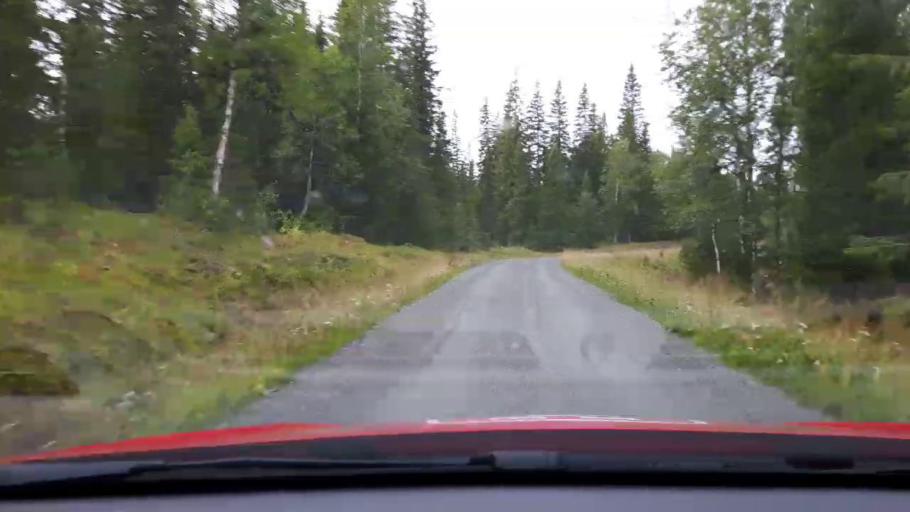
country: SE
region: Jaemtland
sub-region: Are Kommun
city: Are
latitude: 63.7727
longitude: 13.0769
